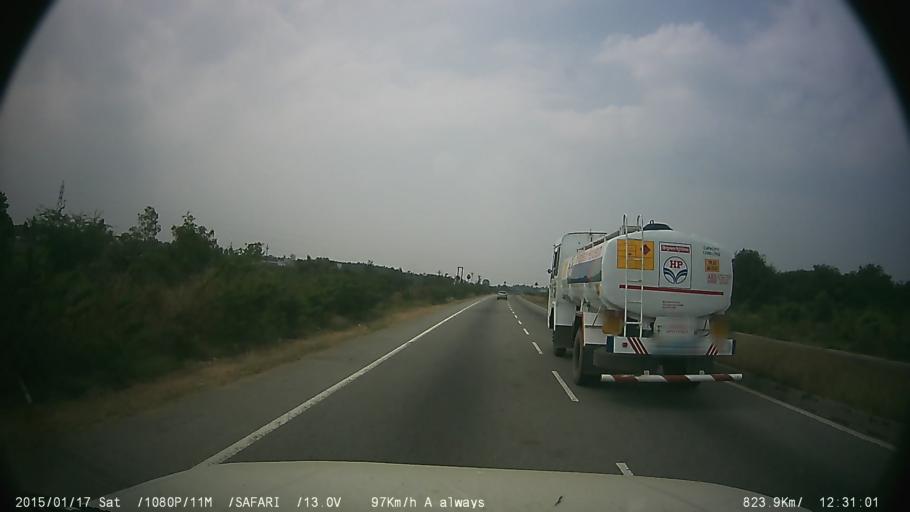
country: IN
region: Tamil Nadu
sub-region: Kancheepuram
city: Kanchipuram
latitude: 12.8731
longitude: 79.6673
